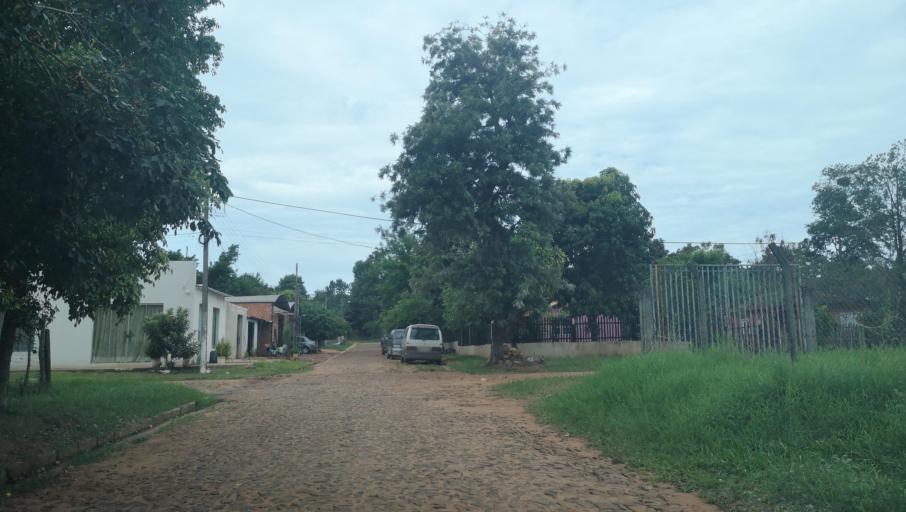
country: PY
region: San Pedro
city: Capiibary
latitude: -24.7344
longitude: -56.0193
